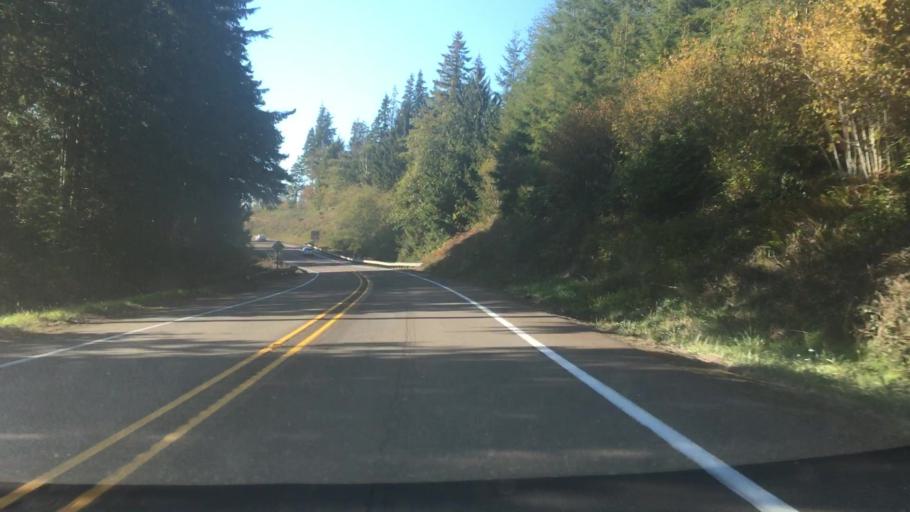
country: US
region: Washington
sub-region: Pacific County
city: South Bend
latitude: 46.6851
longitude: -123.8798
